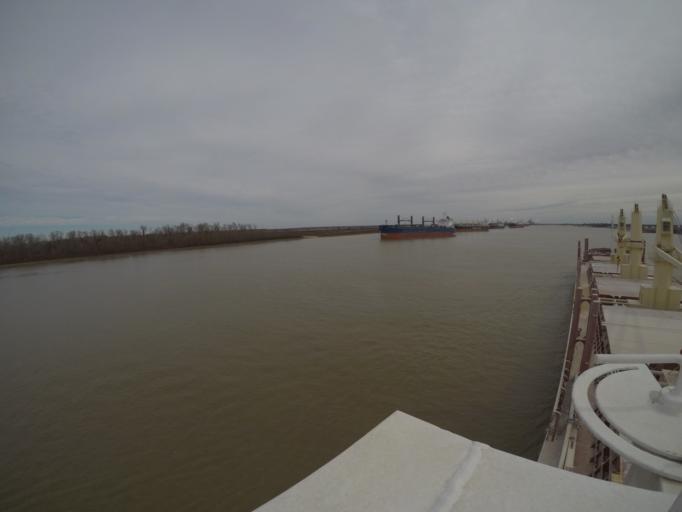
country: US
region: Louisiana
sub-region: Saint Charles Parish
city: Montz
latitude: 29.9961
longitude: -90.4546
